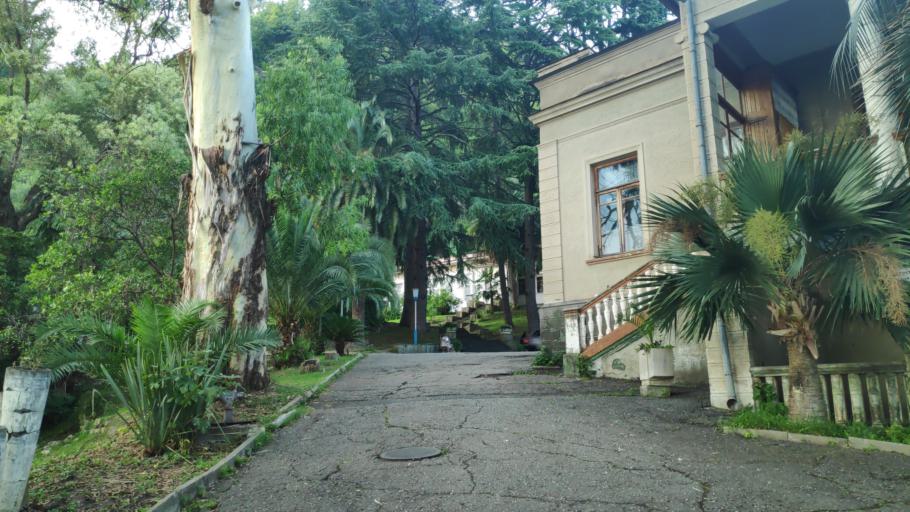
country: GE
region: Abkhazia
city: Stantsiya Novyy Afon
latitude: 43.0881
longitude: 40.8266
